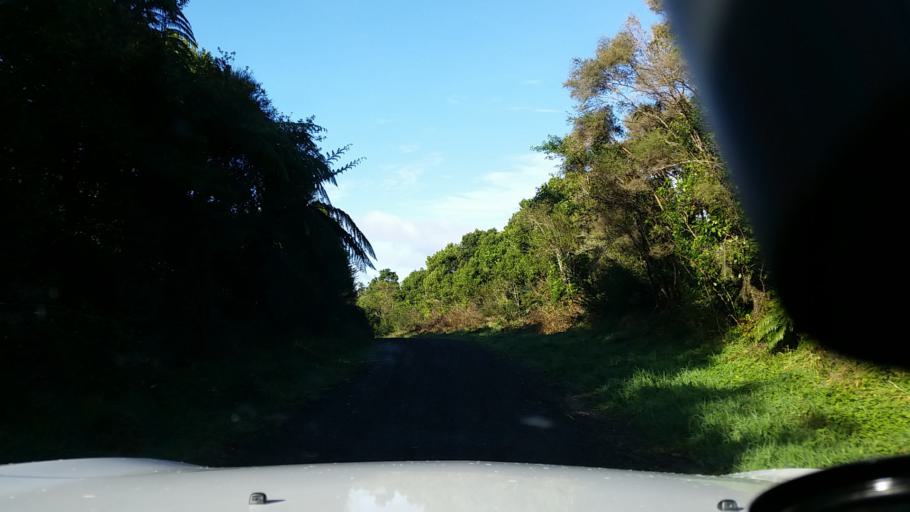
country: NZ
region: Bay of Plenty
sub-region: Kawerau District
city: Kawerau
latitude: -38.0144
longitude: 176.5761
